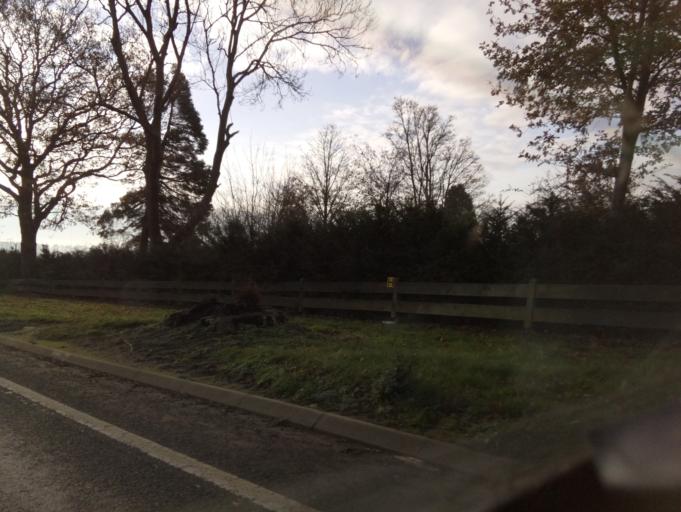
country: GB
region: England
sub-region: City and Borough of Birmingham
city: Sutton Coldfield
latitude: 52.5747
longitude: -1.7680
